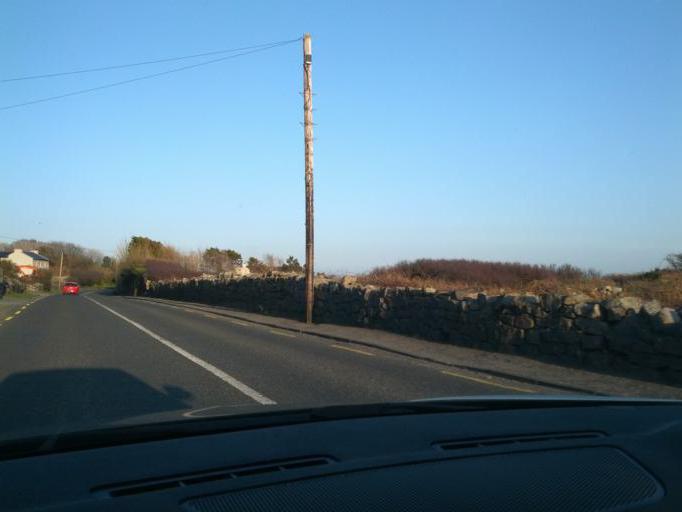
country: IE
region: Connaught
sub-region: County Galway
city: Bearna
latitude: 53.2494
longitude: -9.1987
